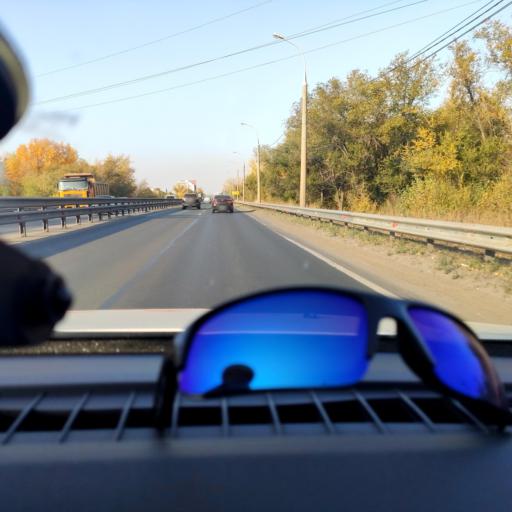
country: RU
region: Samara
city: Samara
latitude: 53.1052
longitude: 50.1632
